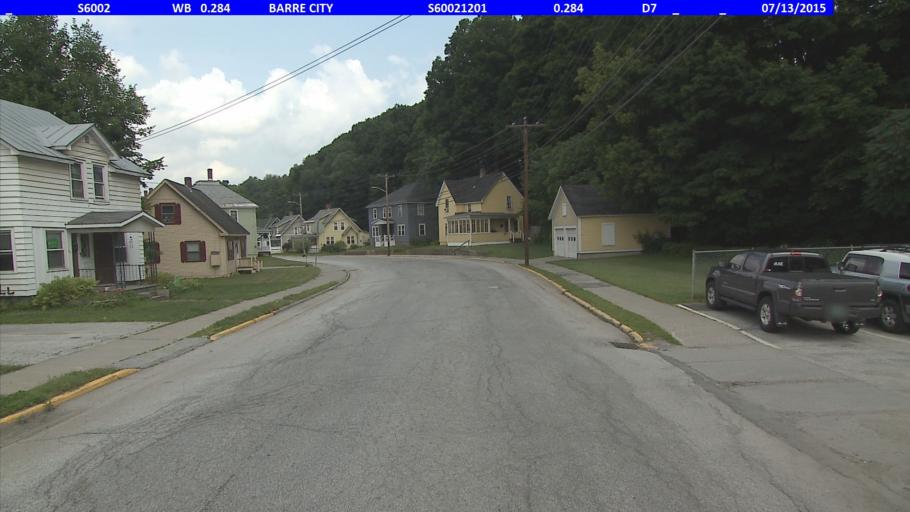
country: US
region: Vermont
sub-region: Washington County
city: Barre
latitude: 44.1902
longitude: -72.4933
